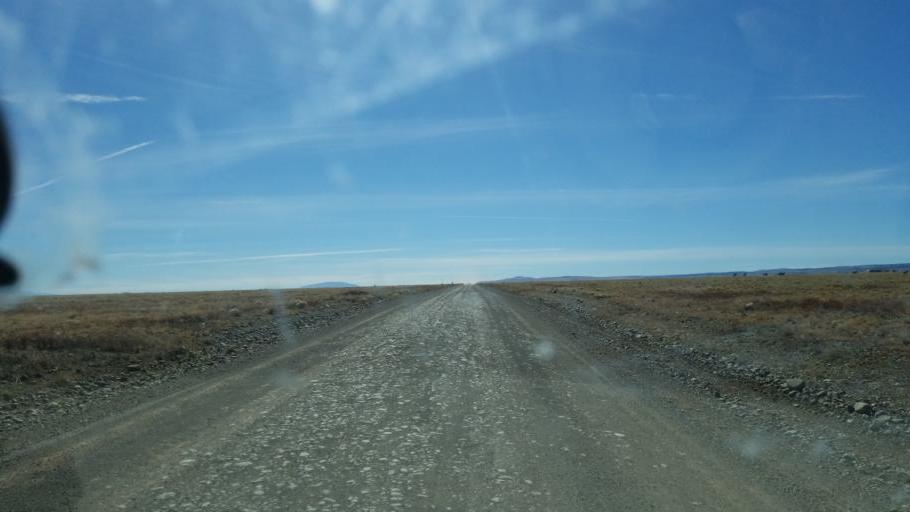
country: US
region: Colorado
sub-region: Rio Grande County
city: Monte Vista
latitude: 37.3641
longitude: -106.1492
